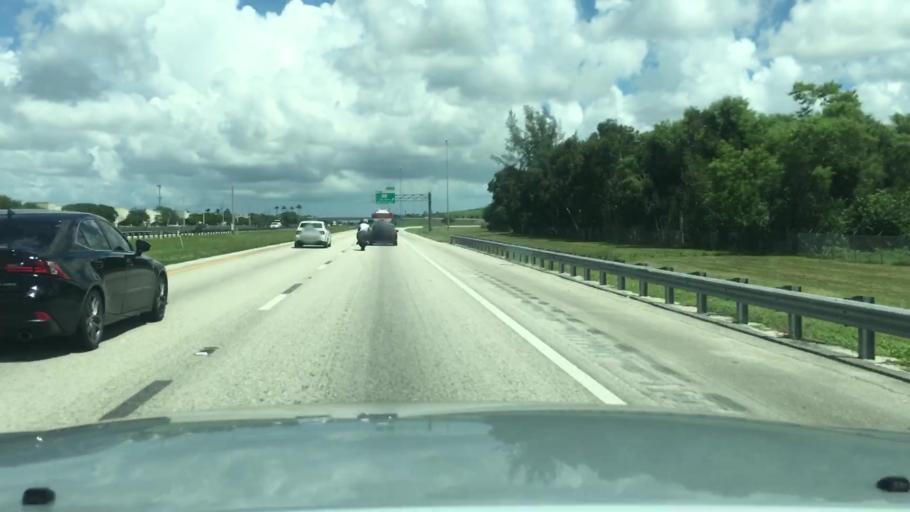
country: US
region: Florida
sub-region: Miami-Dade County
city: Country Club
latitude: 25.9713
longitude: -80.3039
